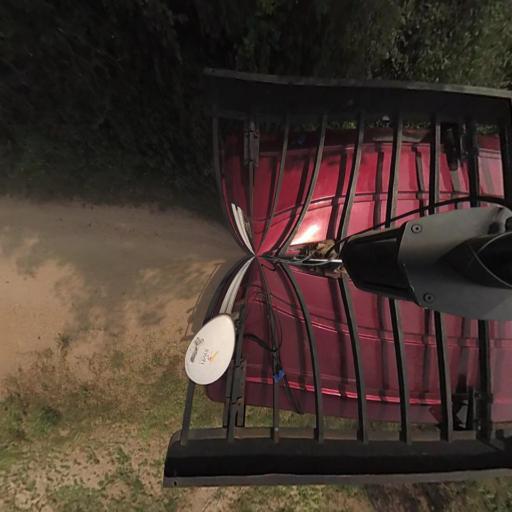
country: IN
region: Telangana
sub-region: Nalgonda
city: Nalgonda
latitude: 17.2073
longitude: 79.1549
